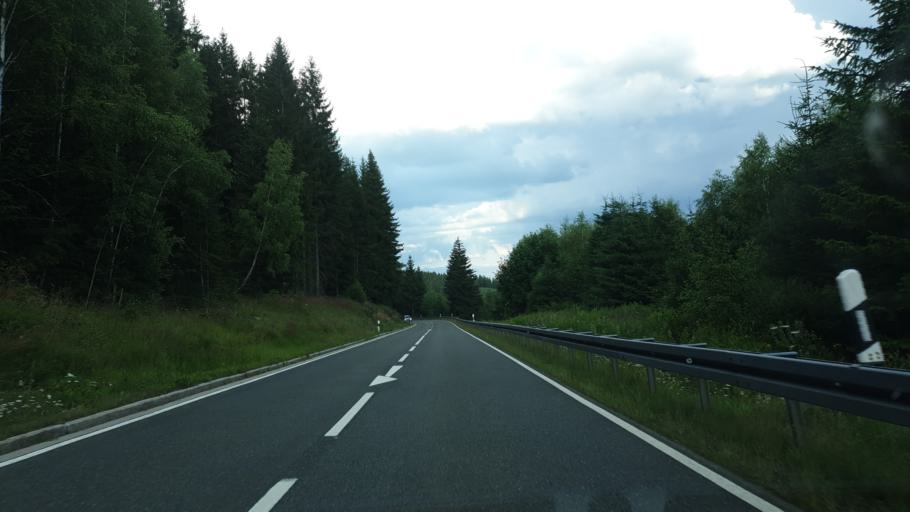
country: DE
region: Saxony
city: Tannenbergsthal
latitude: 50.4537
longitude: 12.4406
